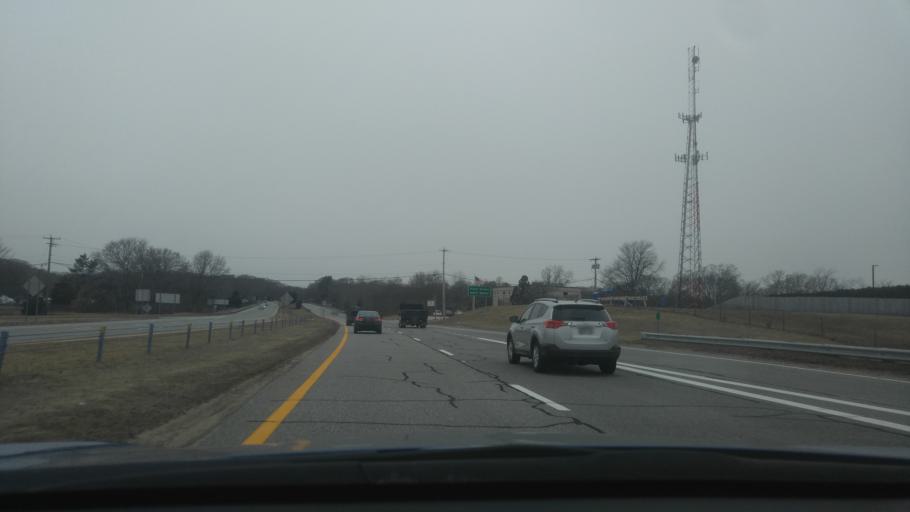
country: US
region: Rhode Island
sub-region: Washington County
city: Wakefield-Peacedale
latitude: 41.4294
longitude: -71.4952
